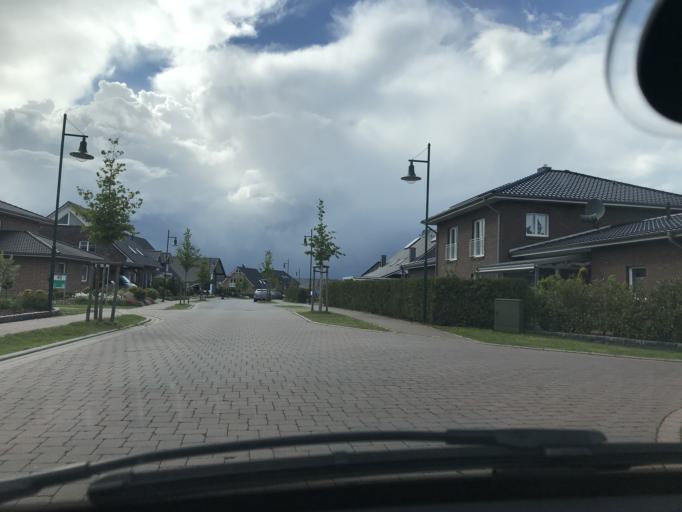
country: DE
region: Lower Saxony
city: Harsefeld
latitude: 53.4440
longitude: 9.5072
